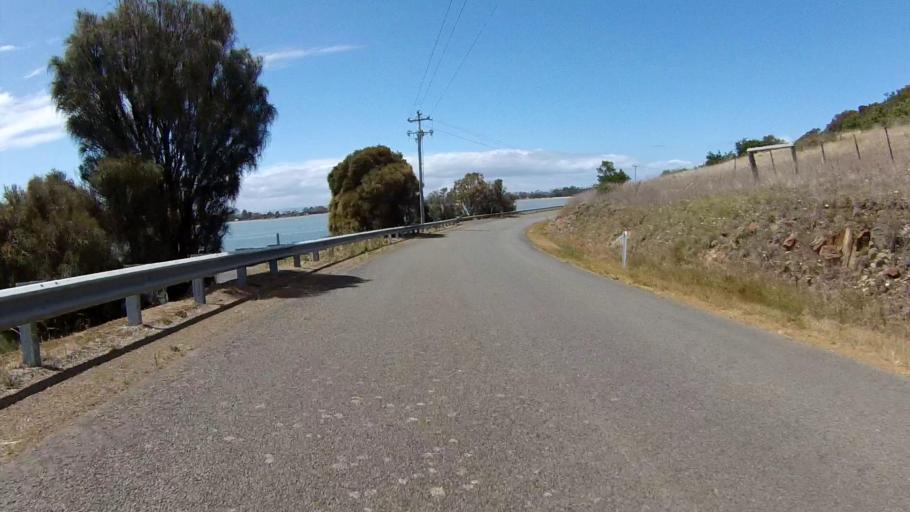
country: AU
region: Tasmania
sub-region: Clarence
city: Lauderdale
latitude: -42.9189
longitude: 147.4745
